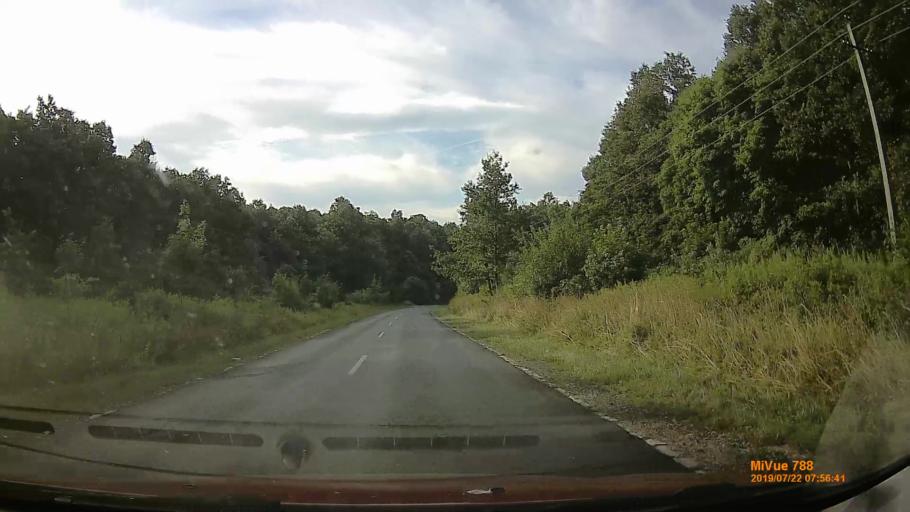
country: HU
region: Veszprem
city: Ajka
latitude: 47.0245
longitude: 17.5730
